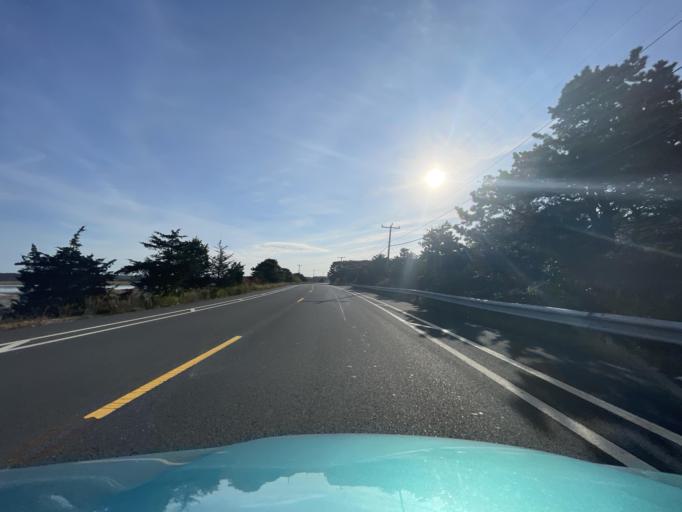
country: US
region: Massachusetts
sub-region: Bristol County
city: Head of Westport
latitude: 41.5098
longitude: -71.0589
